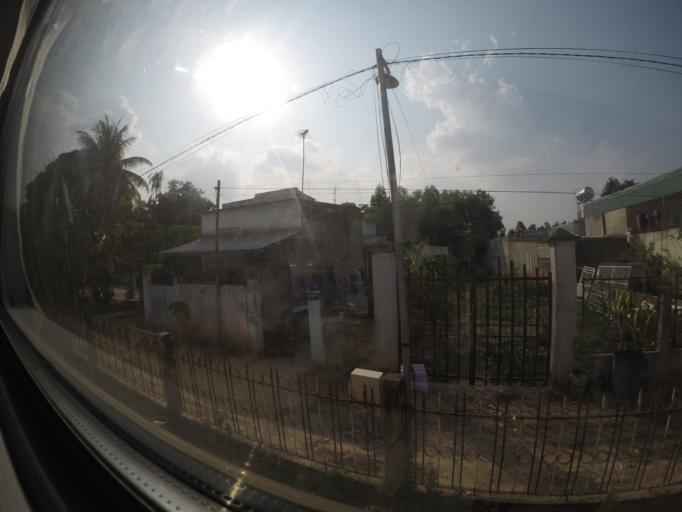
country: VN
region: Binh Duong
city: Di An
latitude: 10.9116
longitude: 106.7723
